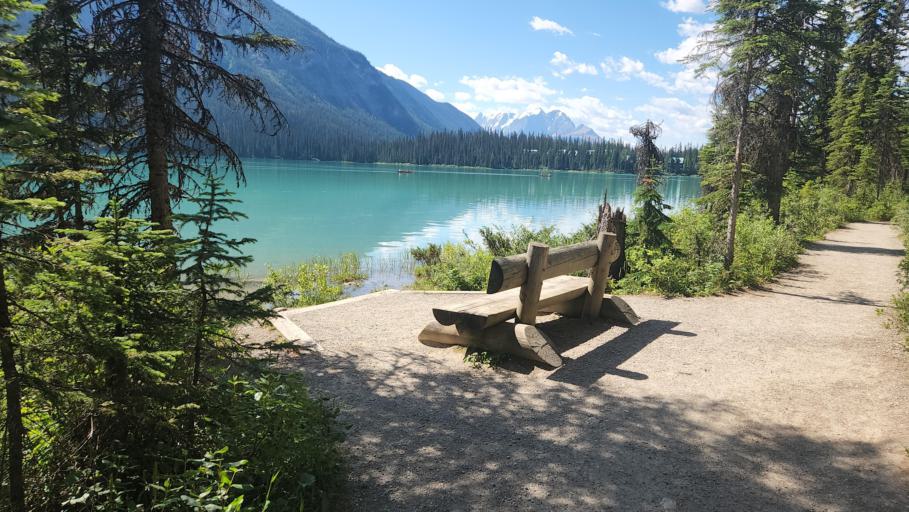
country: CA
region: Alberta
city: Lake Louise
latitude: 51.4463
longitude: -116.5350
